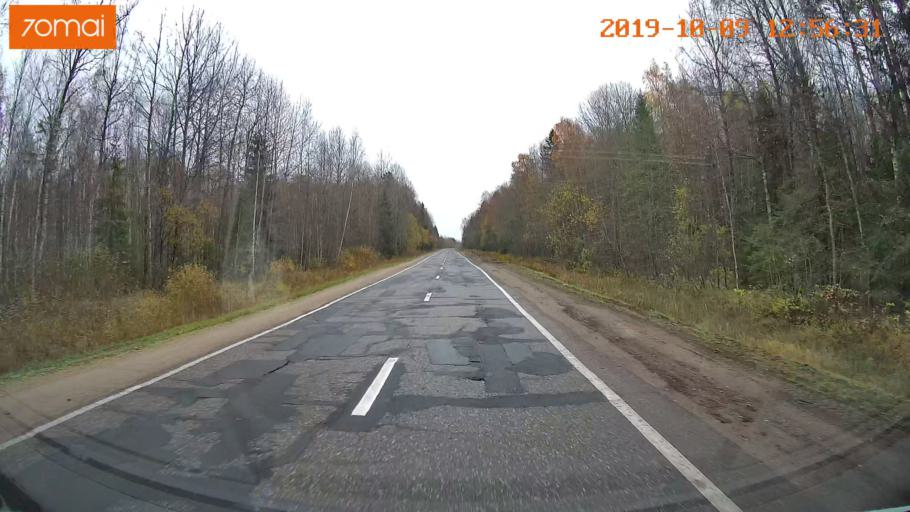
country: RU
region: Jaroslavl
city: Prechistoye
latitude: 58.3947
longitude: 40.4173
